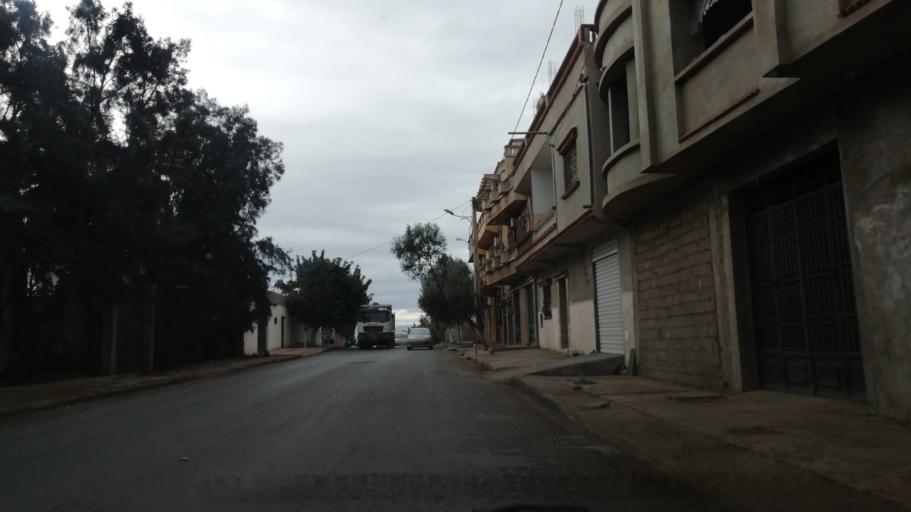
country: DZ
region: Oran
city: Oran
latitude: 35.6945
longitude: -0.5979
